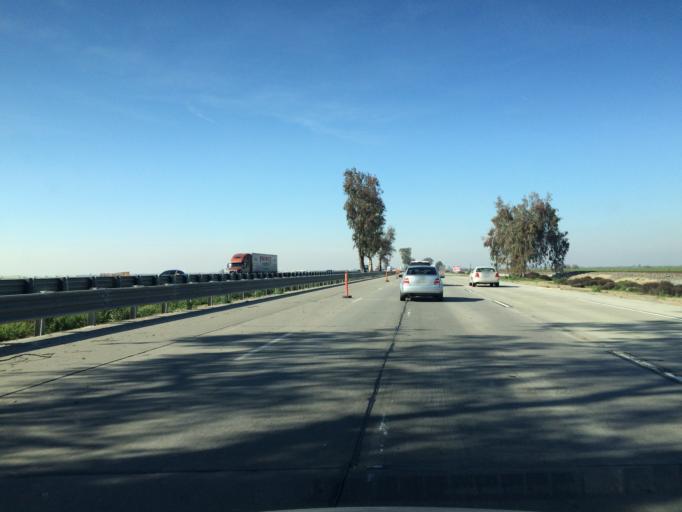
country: US
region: California
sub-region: Tulare County
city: Goshen
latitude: 36.4047
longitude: -119.4565
